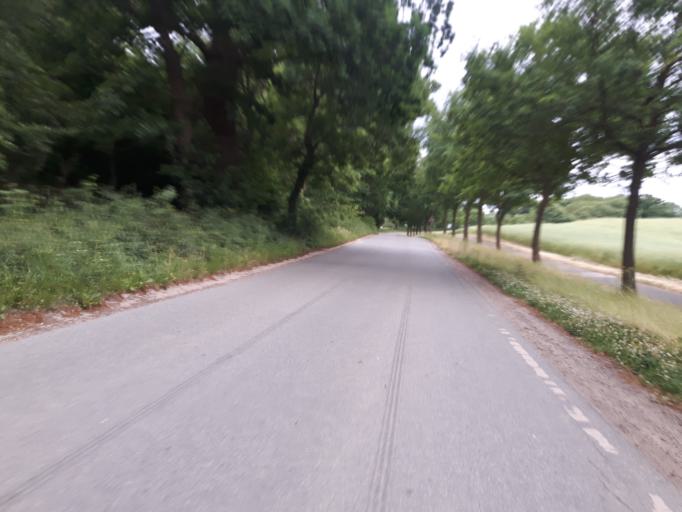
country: DE
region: Schleswig-Holstein
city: Schashagen
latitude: 54.1136
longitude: 10.9009
